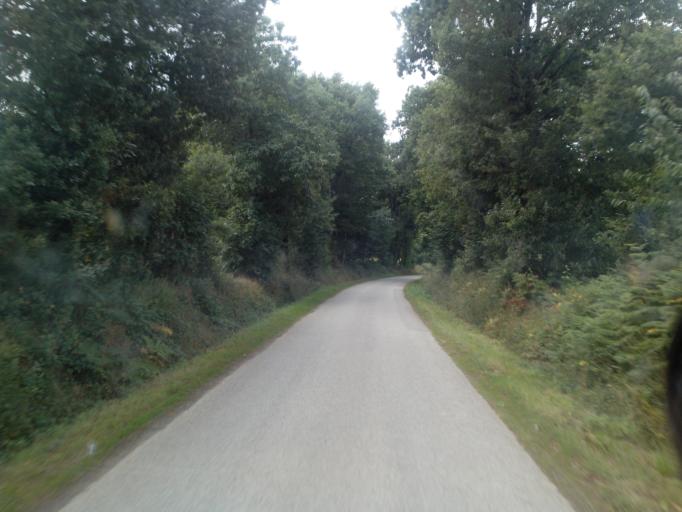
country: FR
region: Brittany
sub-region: Departement du Morbihan
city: Meneac
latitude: 48.1252
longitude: -2.4381
